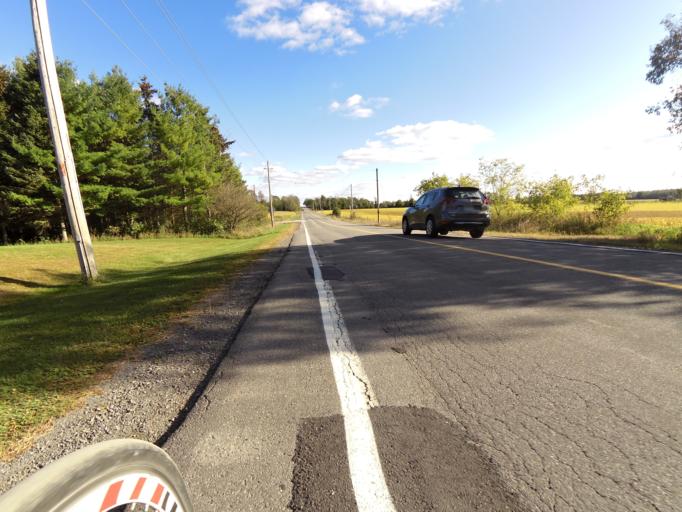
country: CA
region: Ontario
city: Bells Corners
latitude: 45.1091
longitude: -75.7224
